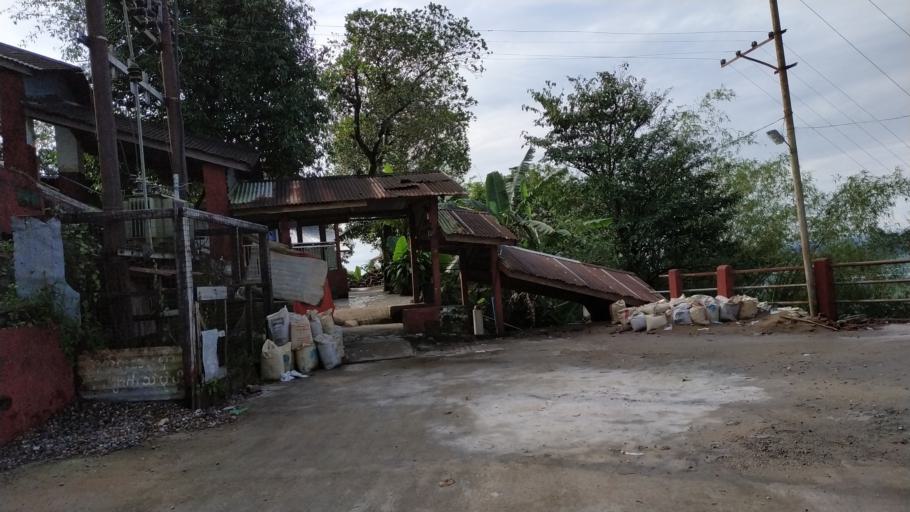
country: MM
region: Mon
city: Thaton
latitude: 16.9253
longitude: 97.3815
